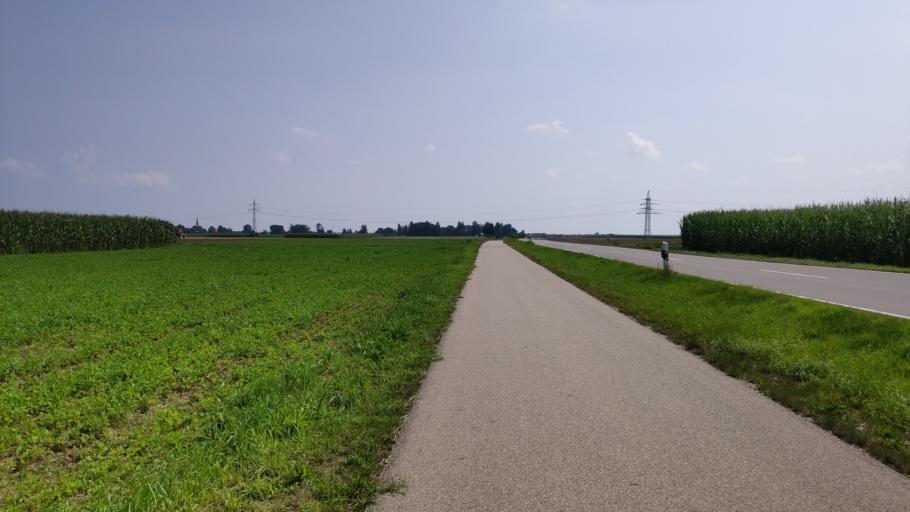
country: DE
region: Bavaria
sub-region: Swabia
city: Kleinaitingen
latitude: 48.2177
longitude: 10.8220
